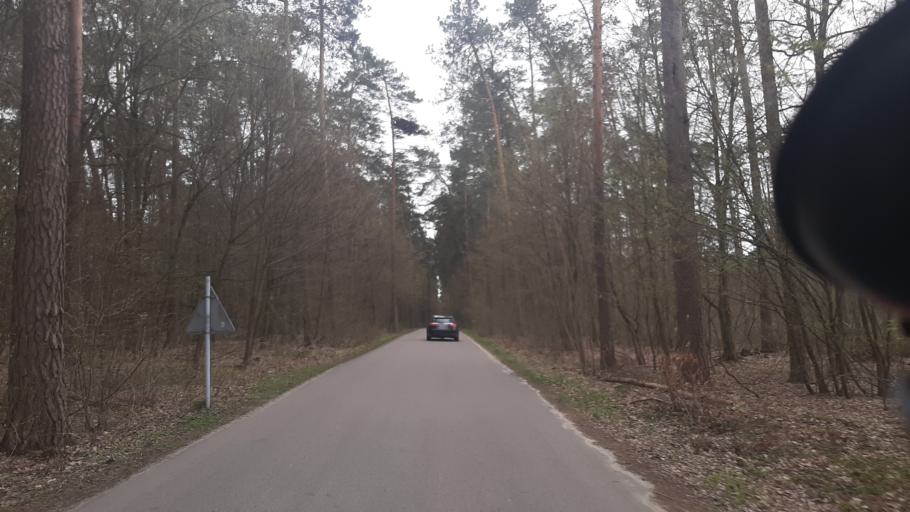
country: PL
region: Lublin Voivodeship
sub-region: Powiat lubelski
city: Niemce
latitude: 51.3751
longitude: 22.5528
